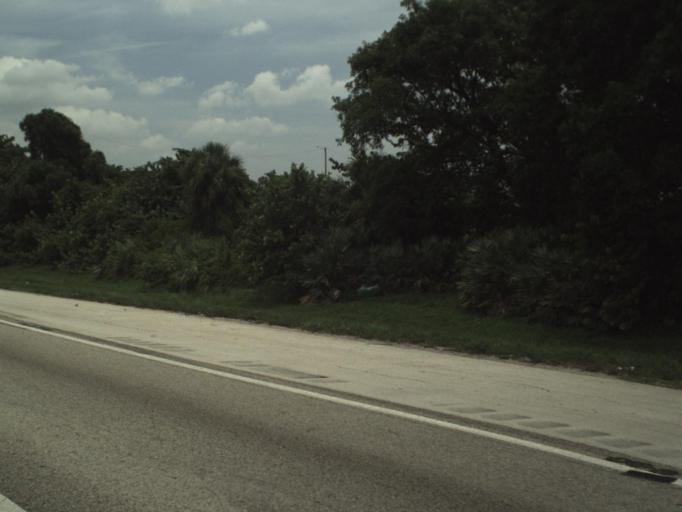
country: US
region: Florida
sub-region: Broward County
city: Pompano Beach
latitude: 26.2251
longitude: -80.1362
